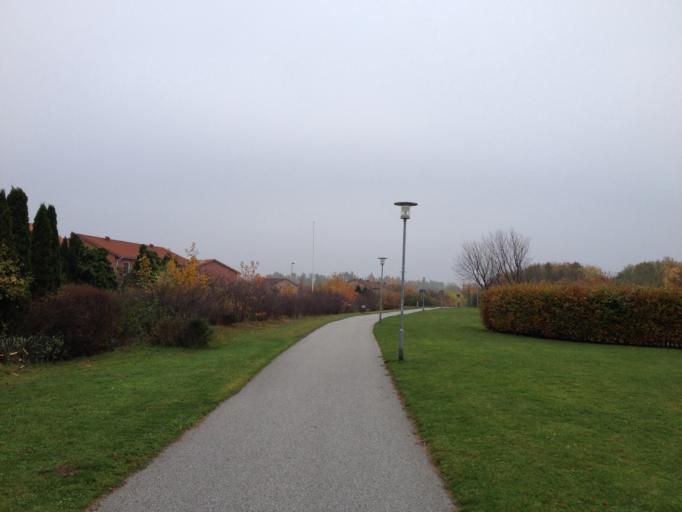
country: SE
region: Skane
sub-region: Burlovs Kommun
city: Arloev
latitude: 55.6066
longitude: 13.0523
